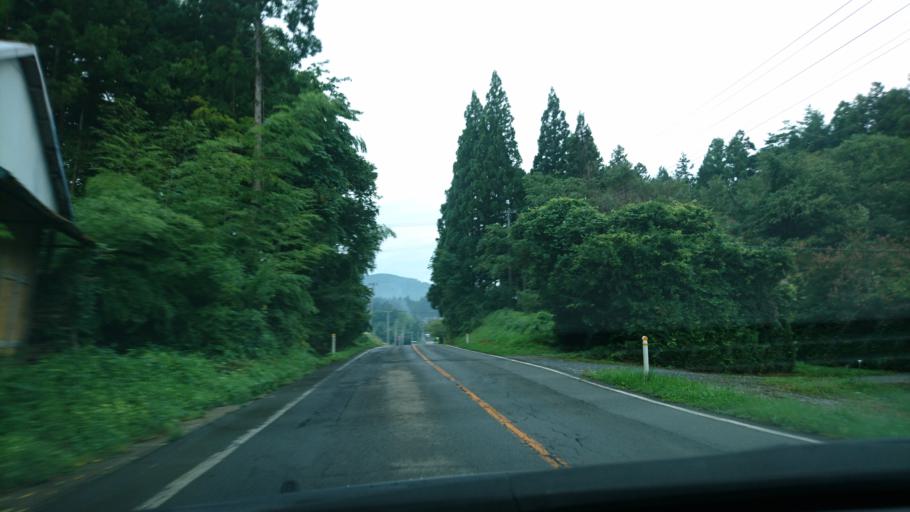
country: JP
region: Iwate
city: Ichinoseki
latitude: 39.0193
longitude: 141.2097
